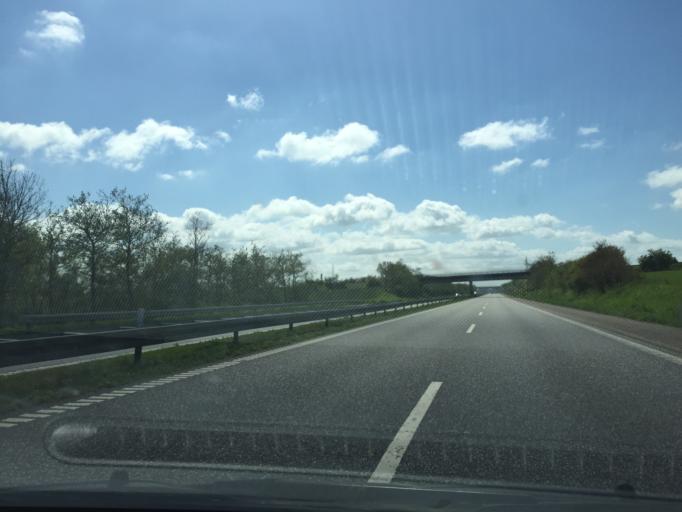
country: DK
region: Zealand
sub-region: Guldborgsund Kommune
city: Norre Alslev
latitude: 54.8730
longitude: 11.8883
